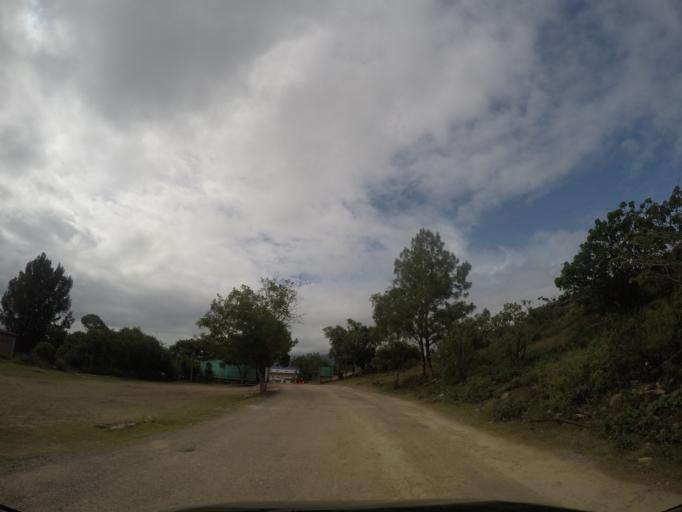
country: MX
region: Oaxaca
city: San Lorenzo Albarradas
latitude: 16.8695
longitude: -96.2769
